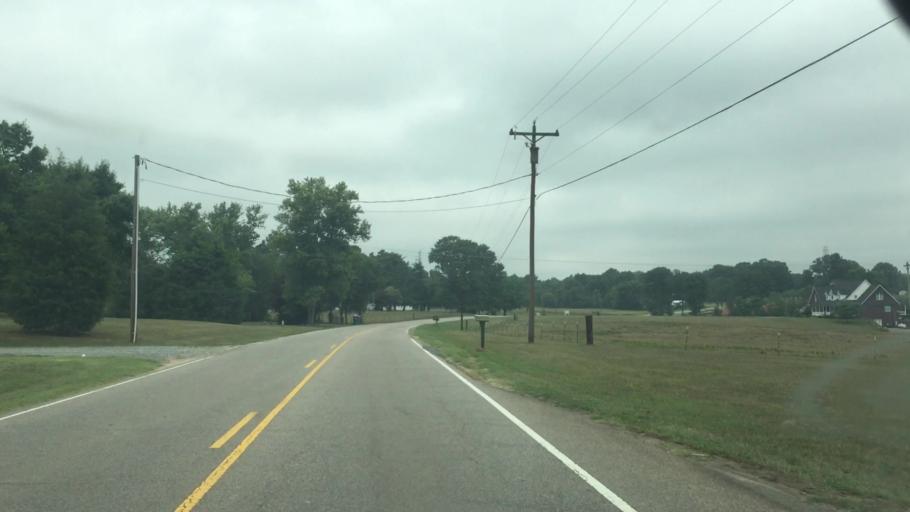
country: US
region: North Carolina
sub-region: Gaston County
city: Davidson
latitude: 35.4951
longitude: -80.7689
